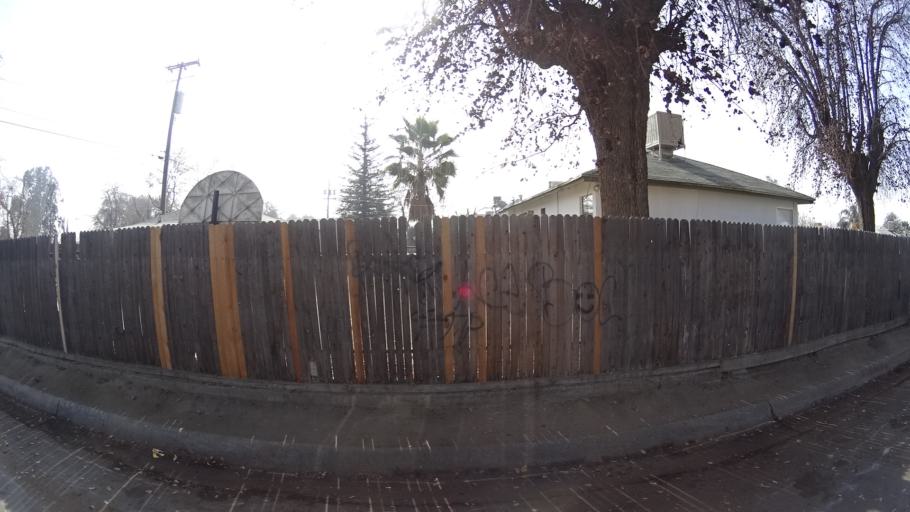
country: US
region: California
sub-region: Kern County
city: Bakersfield
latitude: 35.3430
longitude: -119.0160
